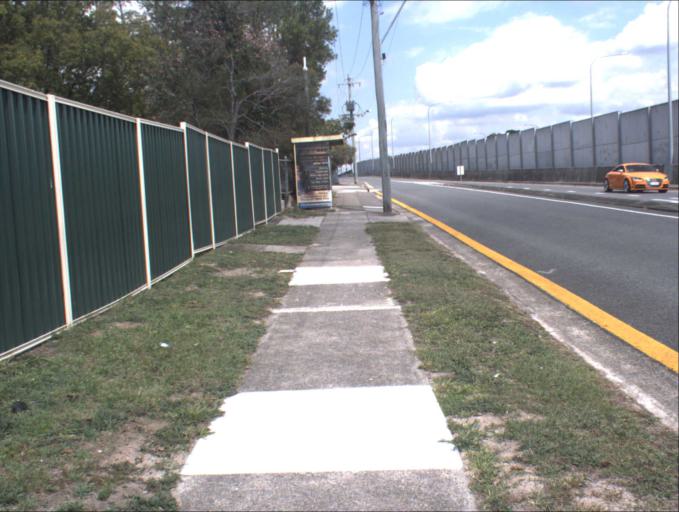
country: AU
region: Queensland
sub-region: Logan
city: Park Ridge South
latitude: -27.7010
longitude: 153.0389
